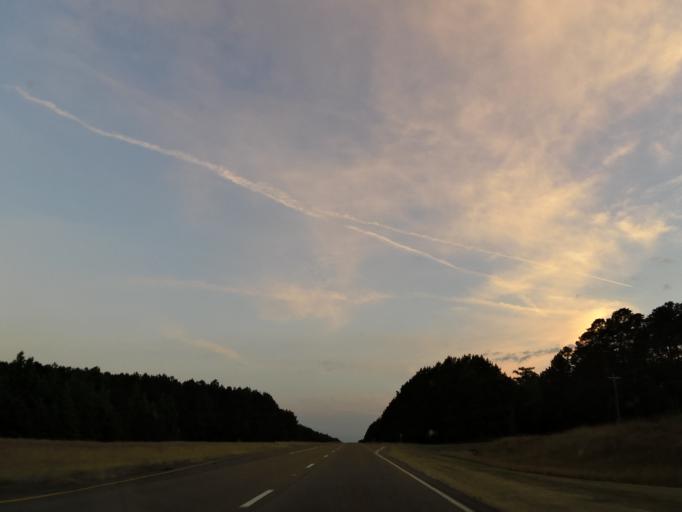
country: US
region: Mississippi
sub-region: Lauderdale County
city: Meridian Station
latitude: 32.6798
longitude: -88.4903
